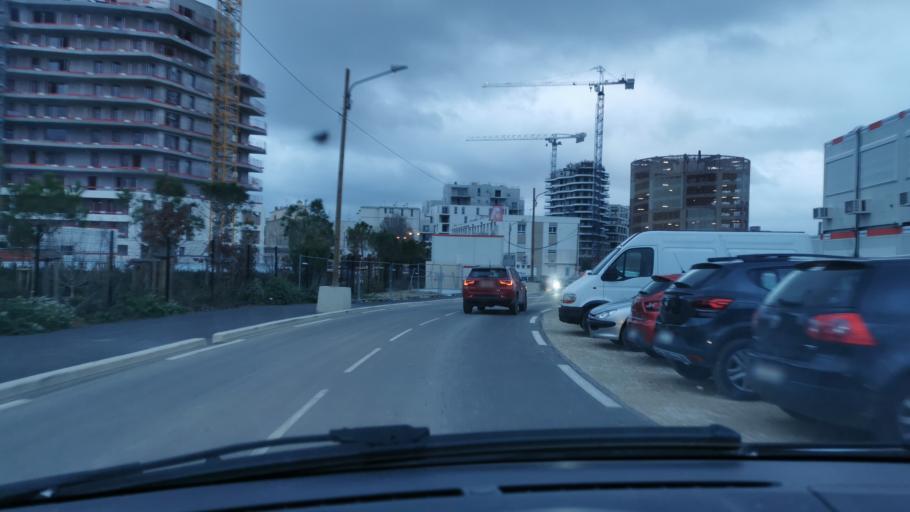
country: FR
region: Languedoc-Roussillon
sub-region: Departement de l'Herault
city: Montpellier
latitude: 43.6013
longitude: 3.8763
